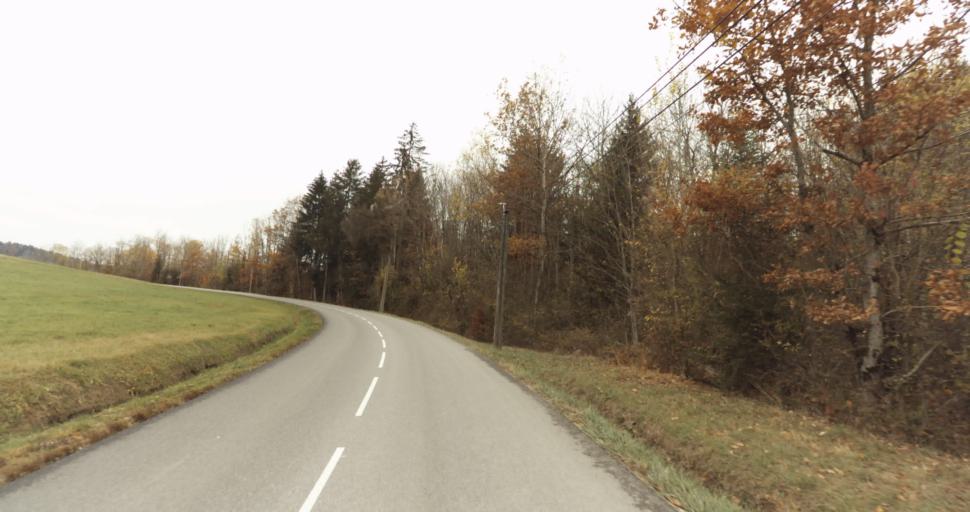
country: FR
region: Rhone-Alpes
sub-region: Departement de la Haute-Savoie
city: Thorens-Glieres
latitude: 45.9861
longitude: 6.2289
